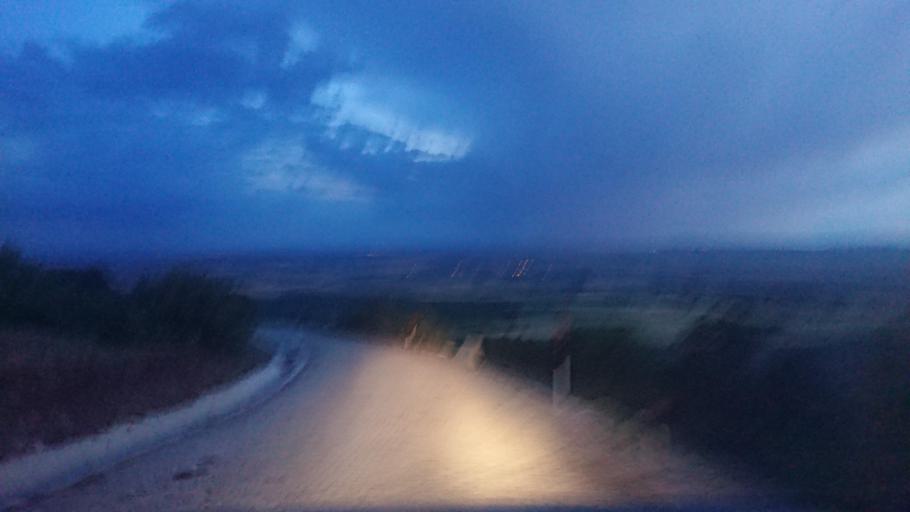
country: TR
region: Aksaray
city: Ortakoy
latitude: 38.6404
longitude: 34.0178
